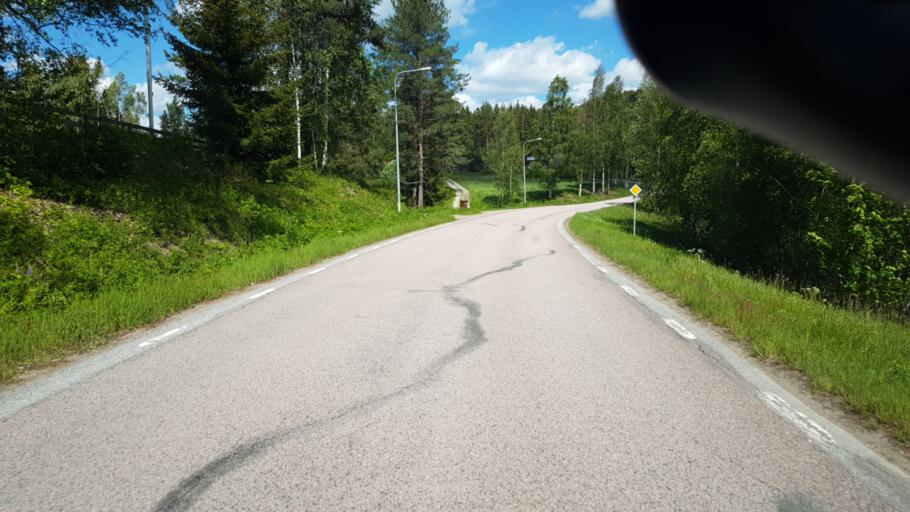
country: SE
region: Vaermland
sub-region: Arvika Kommun
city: Arvika
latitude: 59.6874
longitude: 12.7871
